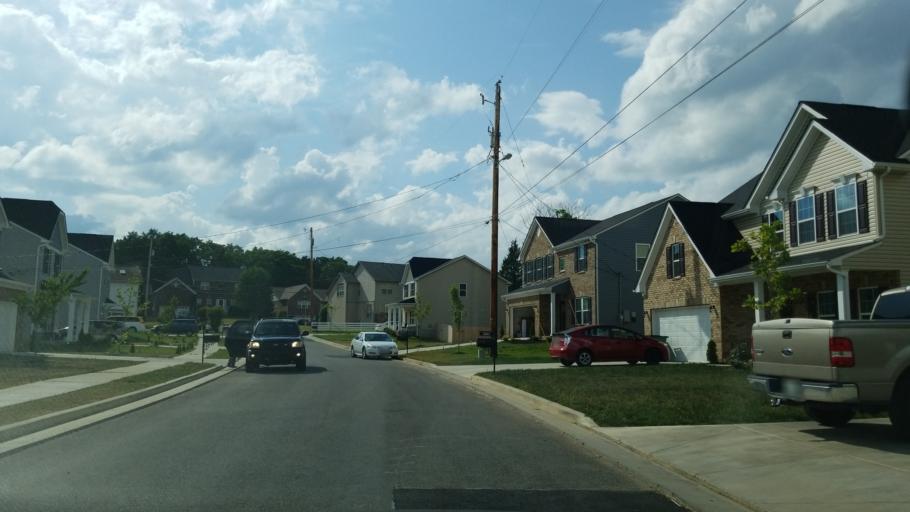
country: US
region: Tennessee
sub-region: Rutherford County
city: La Vergne
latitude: 36.0686
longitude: -86.5915
